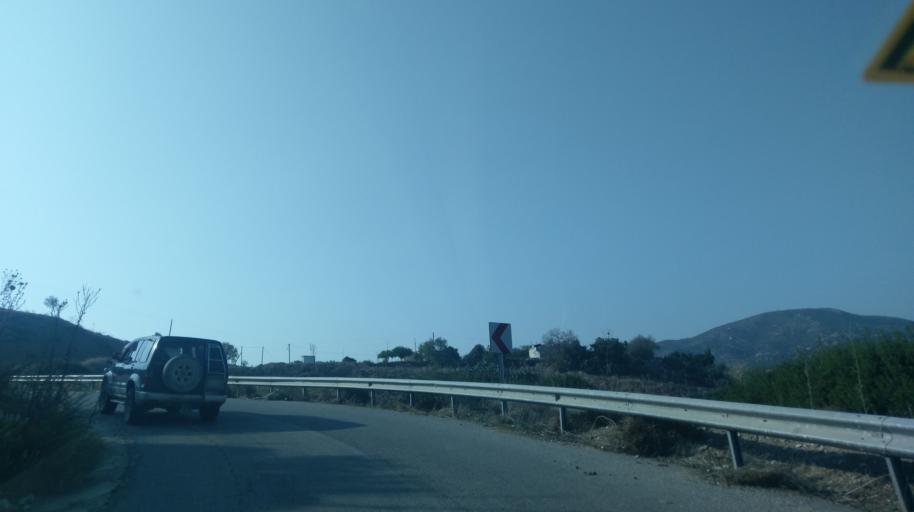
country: CY
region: Ammochostos
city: Rizokarpaso
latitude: 35.5133
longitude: 34.2780
